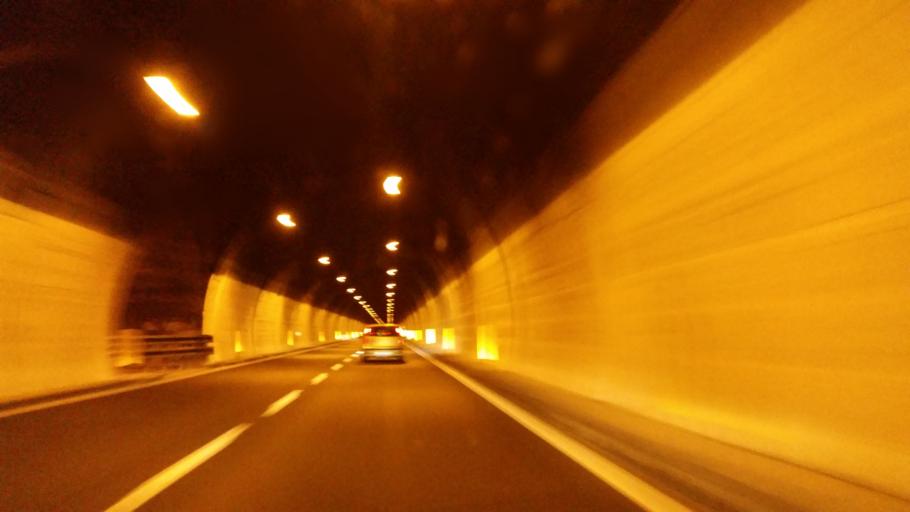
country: IT
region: Liguria
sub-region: Provincia di Imperia
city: Cervo
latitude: 43.9441
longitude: 8.1153
